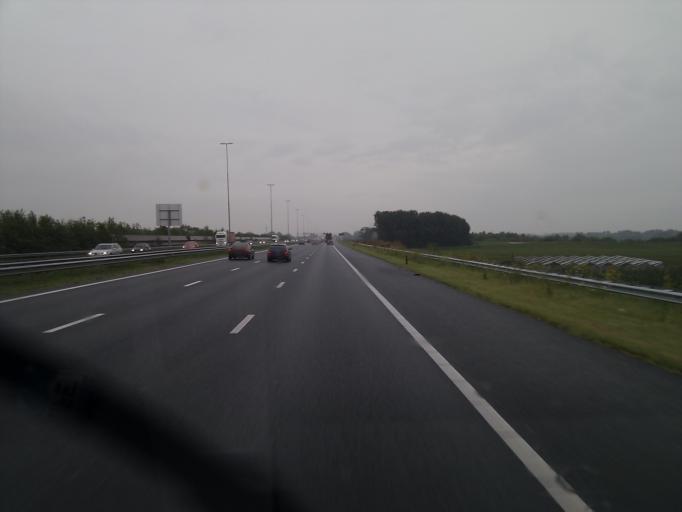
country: NL
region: Gelderland
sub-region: Gemeente Maasdriel
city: Hedel
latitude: 51.7520
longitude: 5.2897
